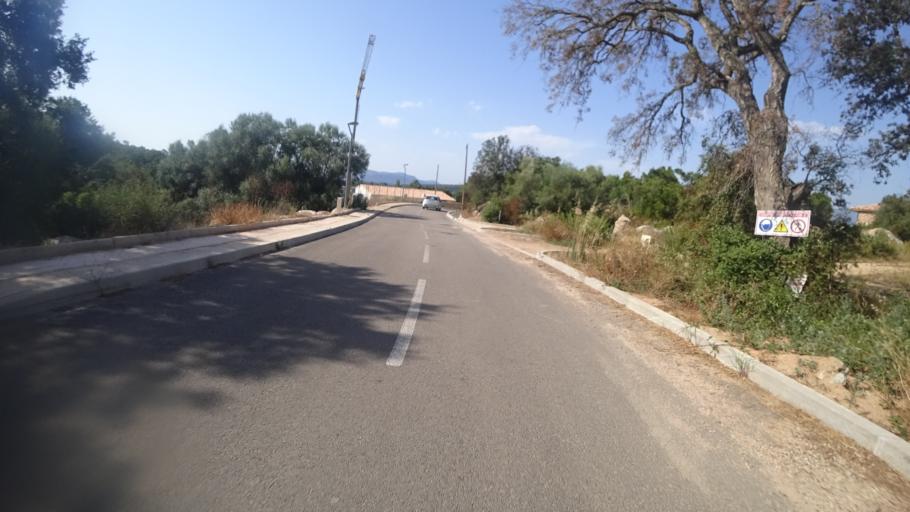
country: FR
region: Corsica
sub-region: Departement de la Corse-du-Sud
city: Porto-Vecchio
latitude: 41.6587
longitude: 9.3255
